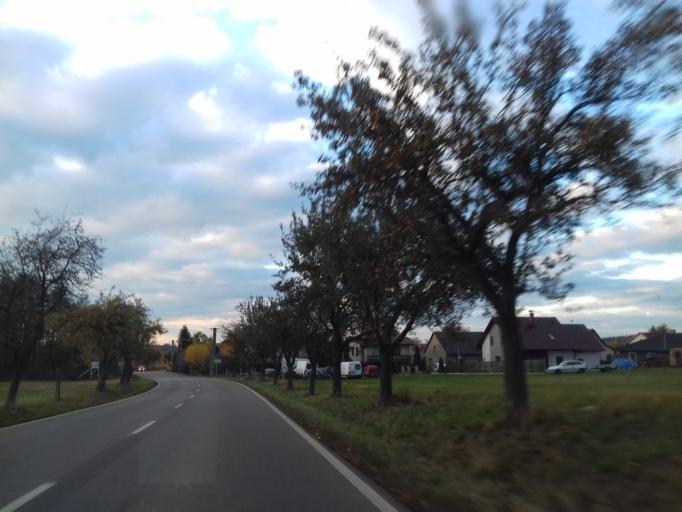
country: CZ
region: Pardubicky
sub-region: Okres Chrudim
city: Skutec
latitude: 49.8279
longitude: 16.0409
